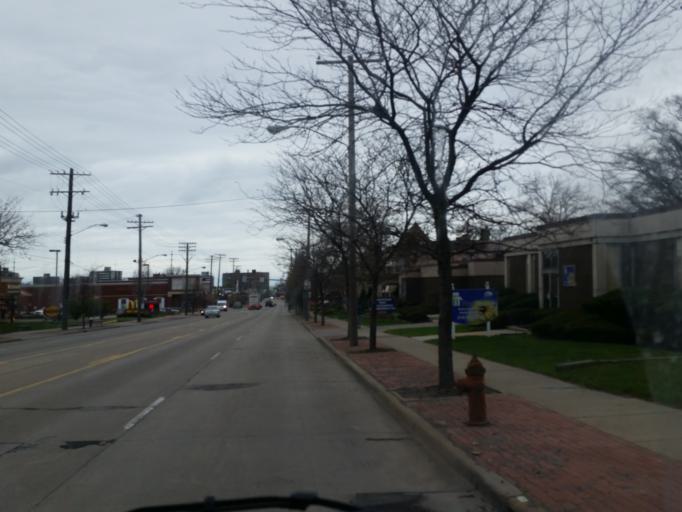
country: US
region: Ohio
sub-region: Cuyahoga County
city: Lakewood
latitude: 41.4817
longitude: -81.7687
